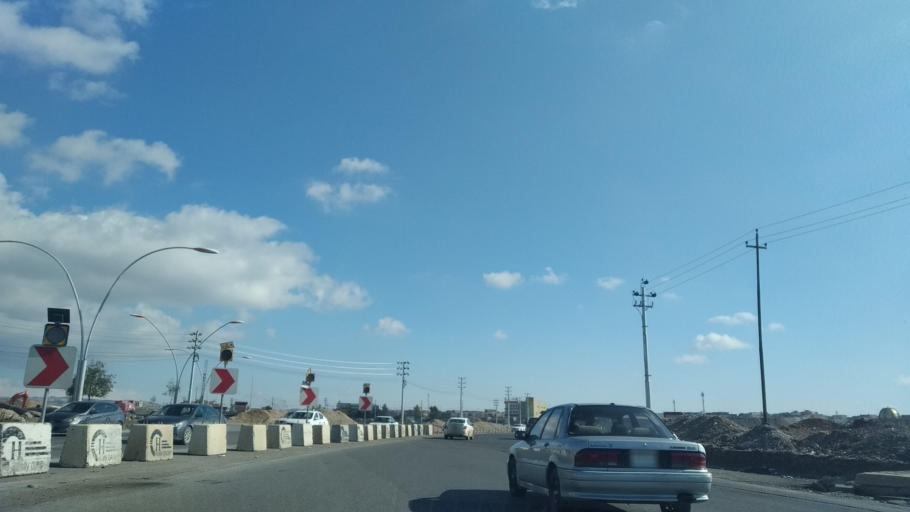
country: IQ
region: Arbil
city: Erbil
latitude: 36.2061
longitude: 44.1262
